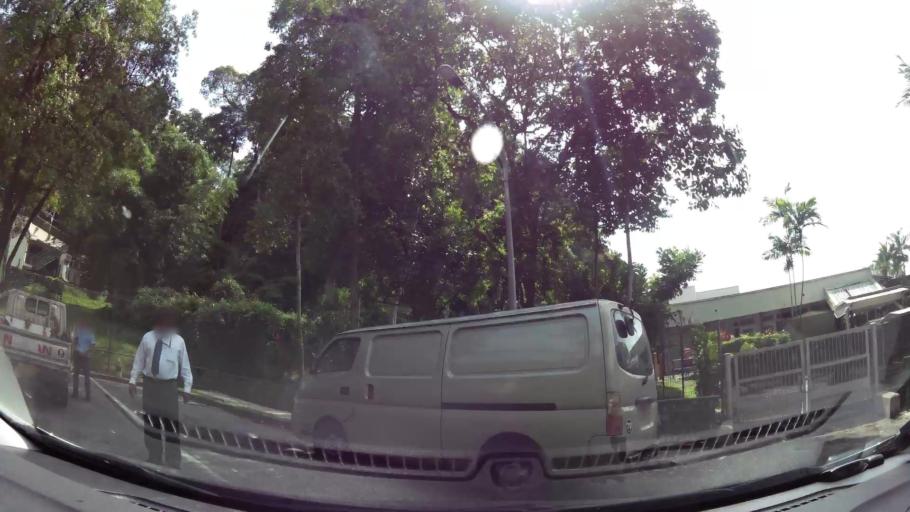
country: SG
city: Singapore
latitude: 1.3461
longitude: 103.7915
